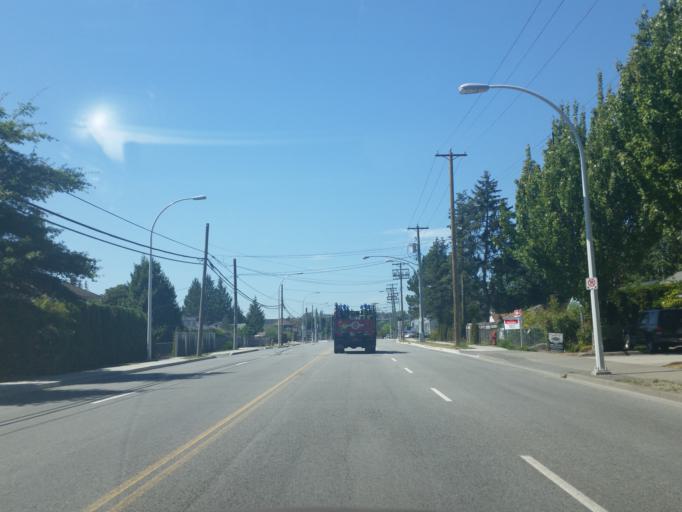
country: CA
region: British Columbia
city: Langley
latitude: 49.1044
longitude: -122.6769
